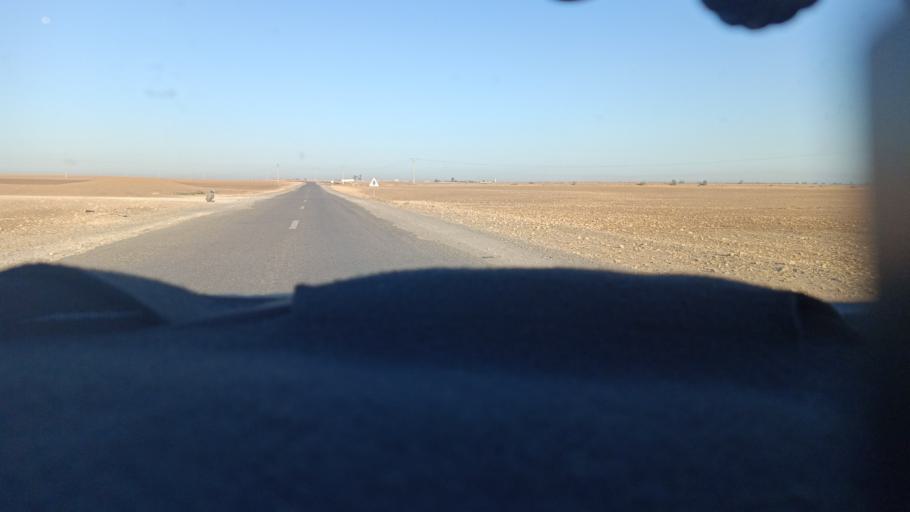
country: MA
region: Doukkala-Abda
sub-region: Safi
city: Youssoufia
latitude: 32.3696
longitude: -8.6273
